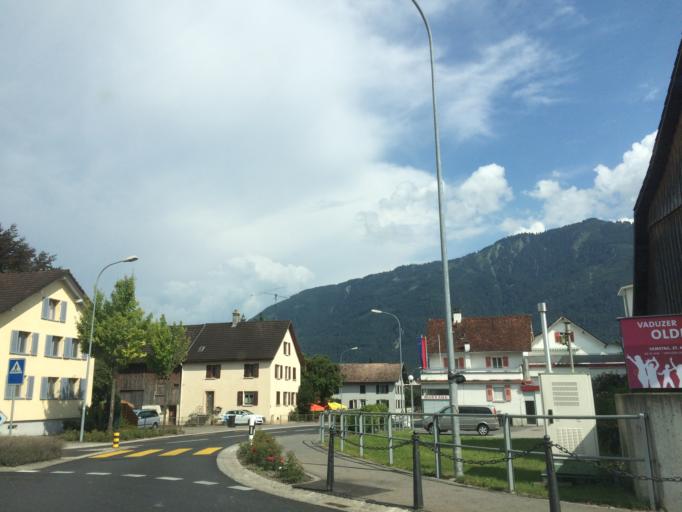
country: LI
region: Eschen
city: Eschen
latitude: 47.2094
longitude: 9.5219
